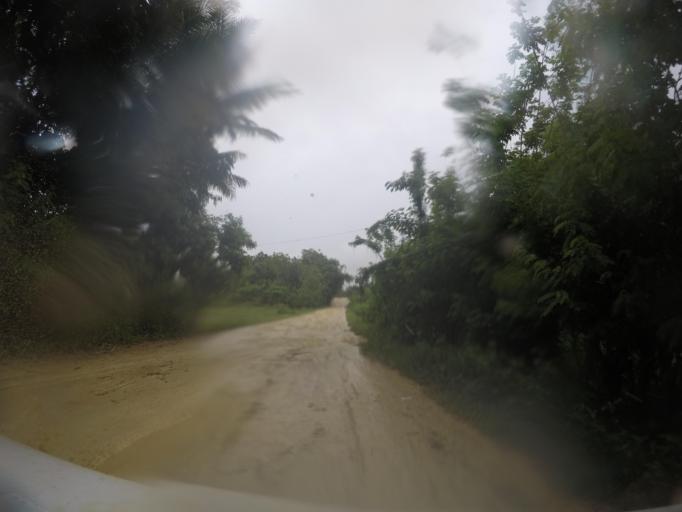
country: TL
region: Lautem
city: Lospalos
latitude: -8.4970
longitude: 126.9943
